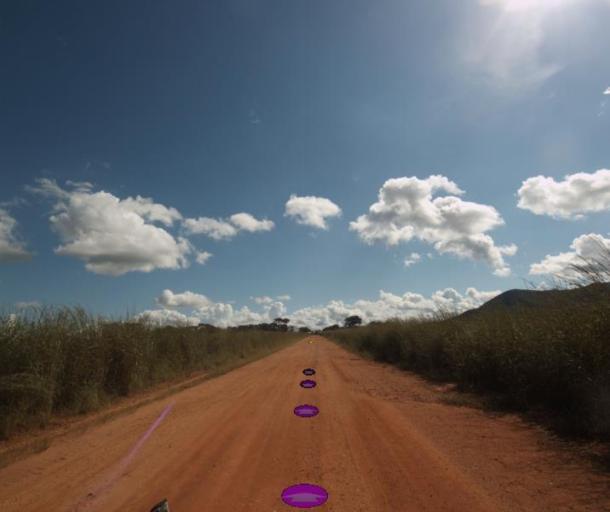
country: BR
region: Goias
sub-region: Jaragua
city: Jaragua
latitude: -15.8353
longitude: -49.2700
